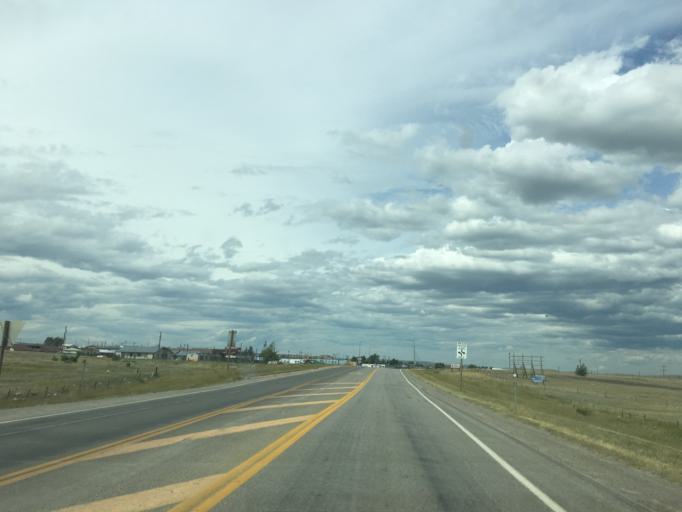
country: US
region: Montana
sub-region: Glacier County
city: South Browning
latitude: 48.5454
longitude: -113.0093
